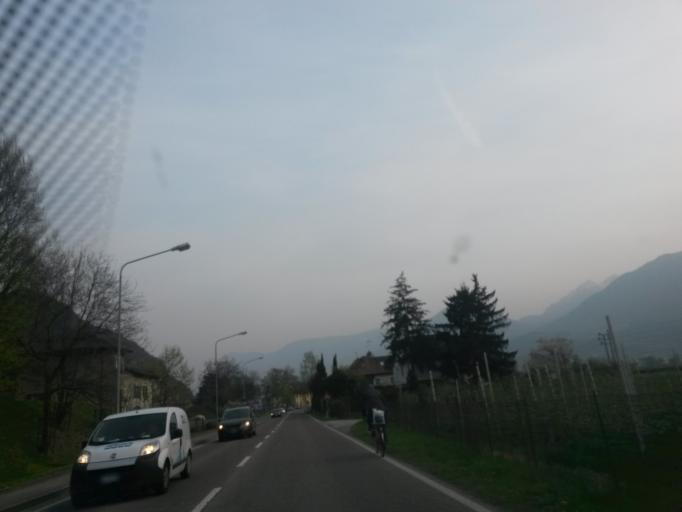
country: IT
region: Trentino-Alto Adige
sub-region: Bolzano
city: Sinigo
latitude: 46.6439
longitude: 11.1774
